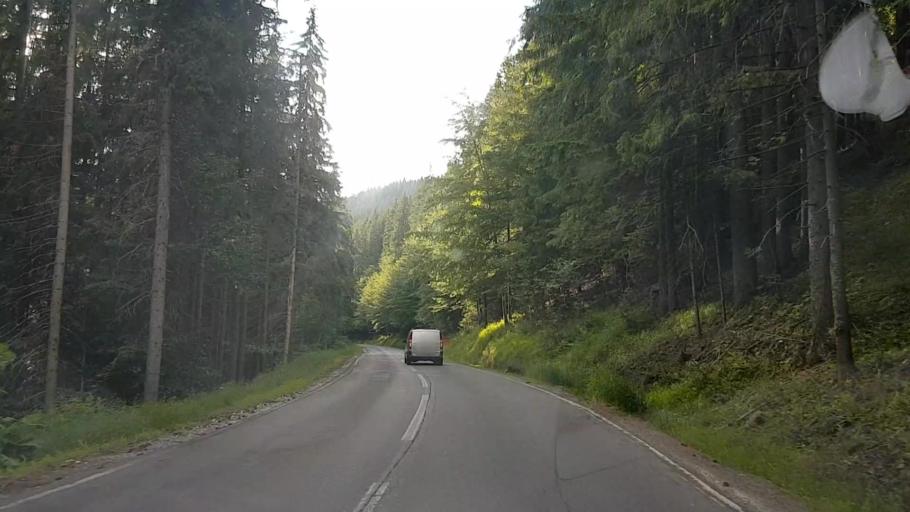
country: RO
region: Harghita
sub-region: Comuna Varsag
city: Varsag
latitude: 46.6639
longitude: 25.3151
